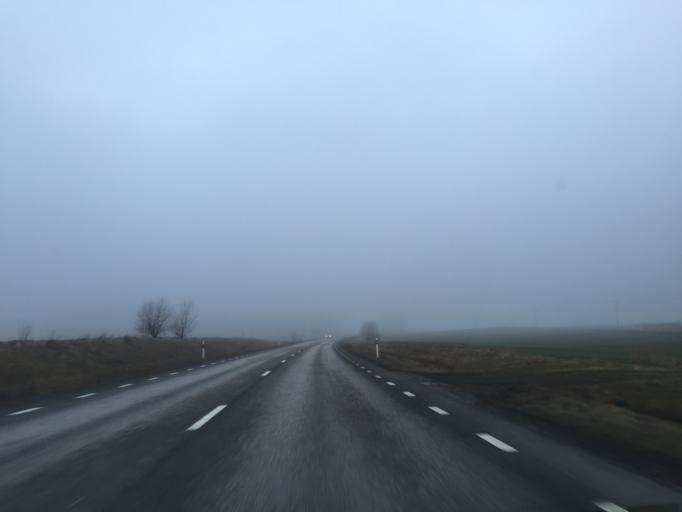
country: SE
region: Soedermanland
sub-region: Nykopings Kommun
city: Olstorp
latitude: 58.8982
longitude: 16.6400
